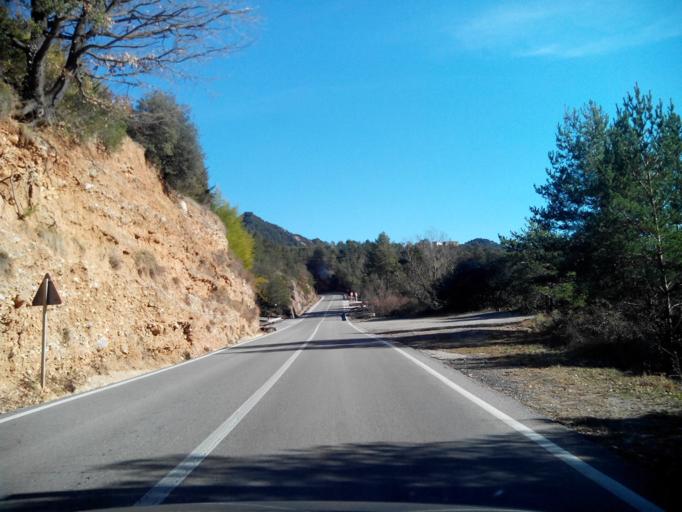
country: ES
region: Catalonia
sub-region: Provincia de Barcelona
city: Berga
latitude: 42.1246
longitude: 1.8699
